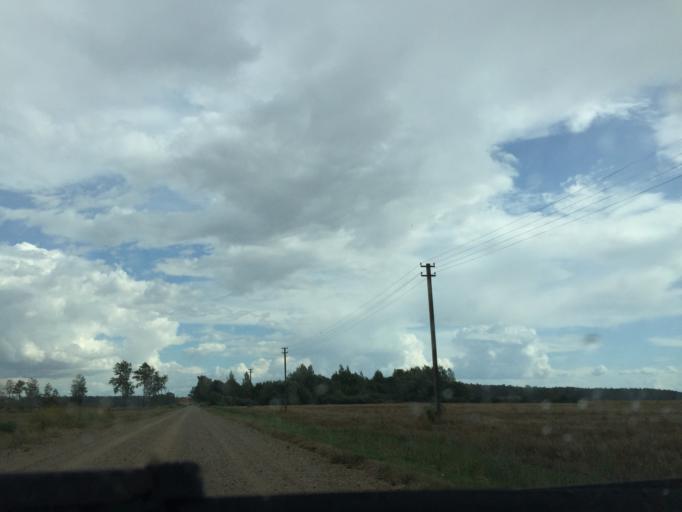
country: LT
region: Siauliu apskritis
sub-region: Joniskis
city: Joniskis
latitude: 56.3504
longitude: 23.5380
